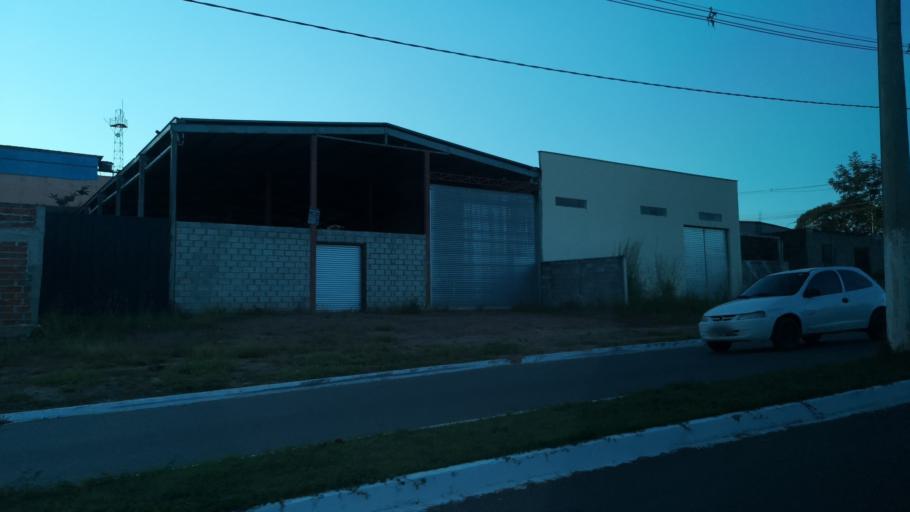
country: BR
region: Goias
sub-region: Goiania
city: Goiania
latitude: -16.6907
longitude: -49.1871
